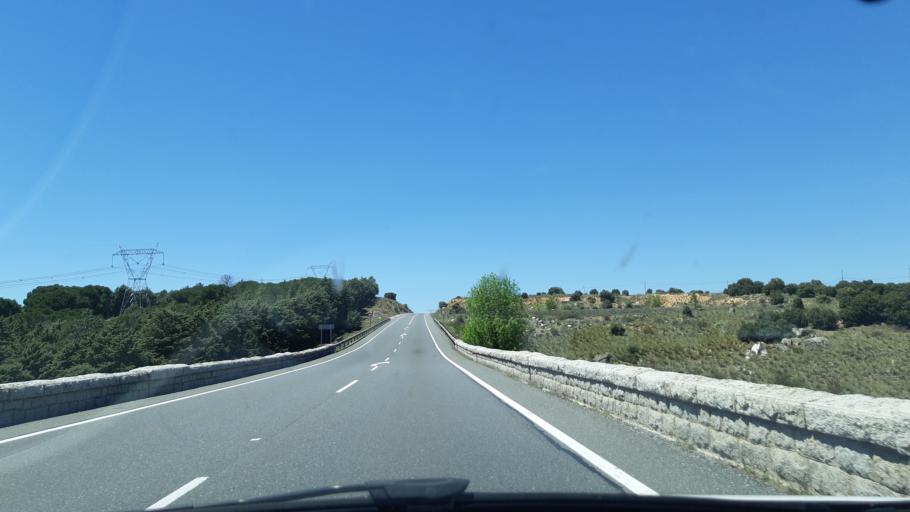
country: ES
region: Castille and Leon
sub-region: Provincia de Segovia
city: Ituero y Lama
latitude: 40.7720
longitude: -4.3767
